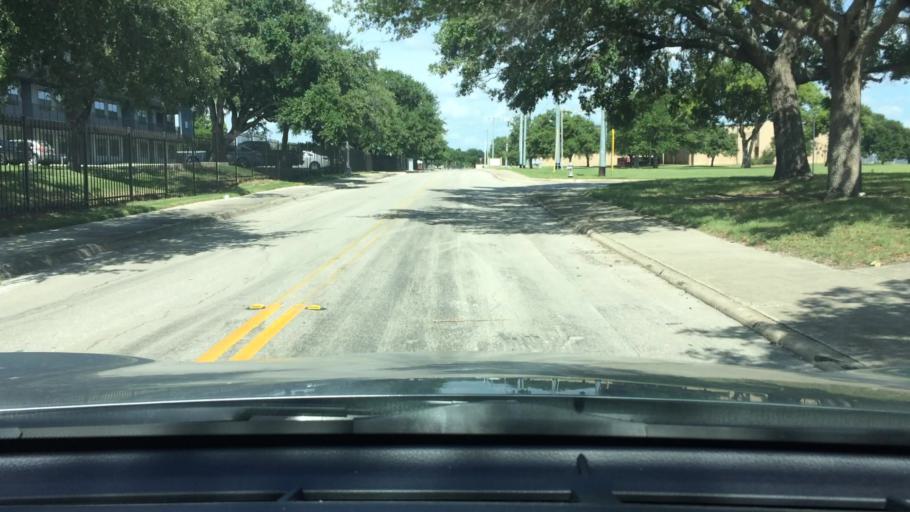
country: US
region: Texas
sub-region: Bexar County
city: San Antonio
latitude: 29.3416
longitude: -98.4488
